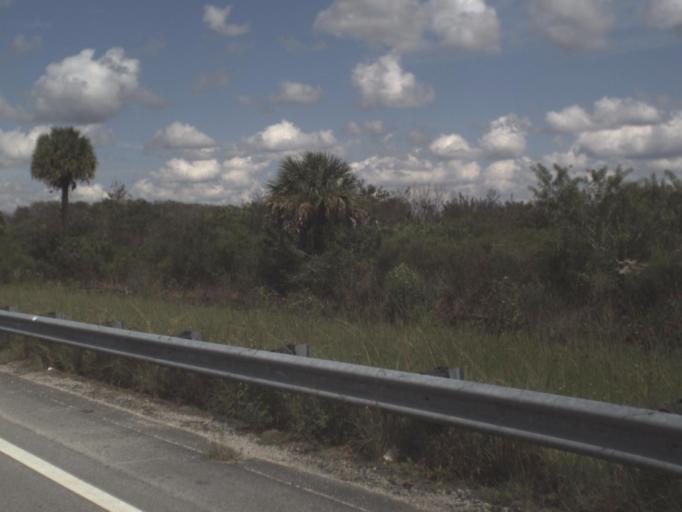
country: US
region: Florida
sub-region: Collier County
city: Immokalee
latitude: 26.1481
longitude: -81.3450
